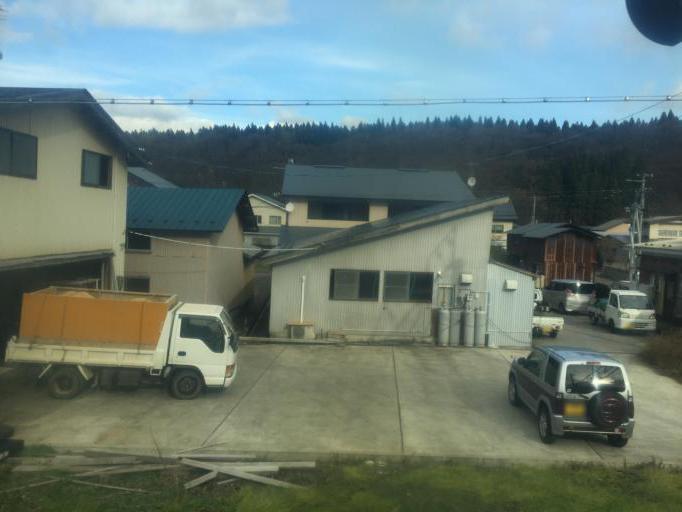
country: JP
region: Akita
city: Noshiromachi
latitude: 40.2035
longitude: 140.1203
